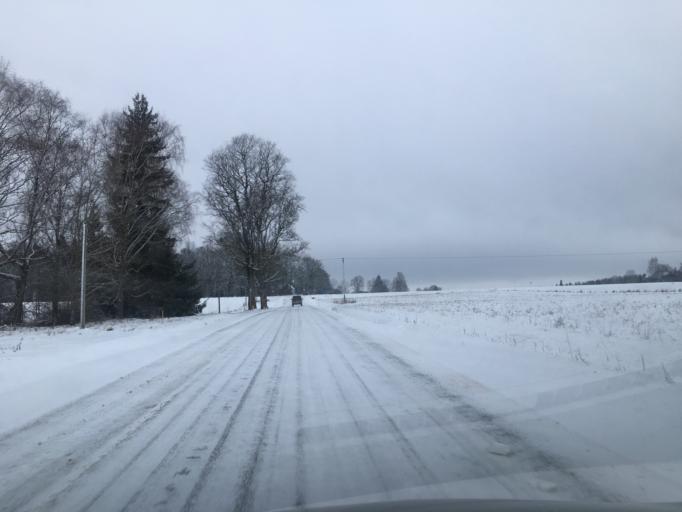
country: EE
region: Tartu
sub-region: Puhja vald
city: Puhja
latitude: 58.1902
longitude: 26.2114
